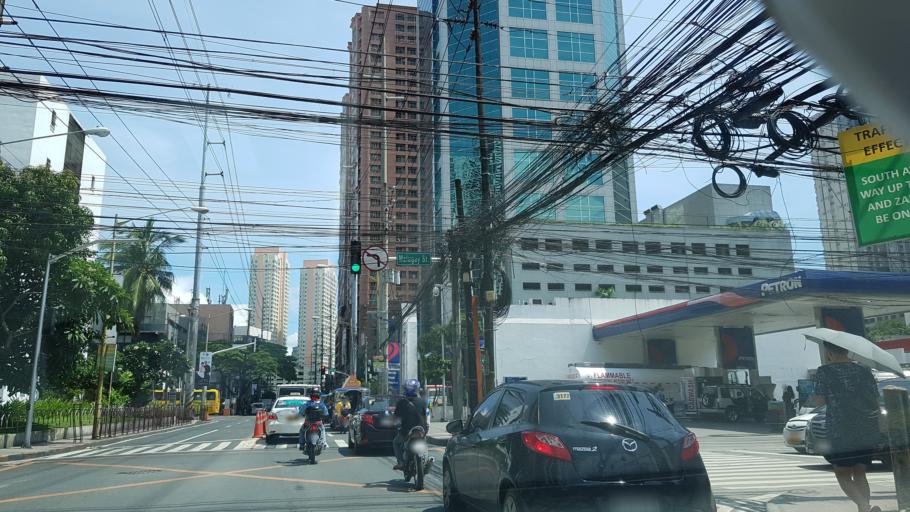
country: PH
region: Metro Manila
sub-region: Makati City
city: Makati City
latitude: 14.5607
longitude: 121.0113
